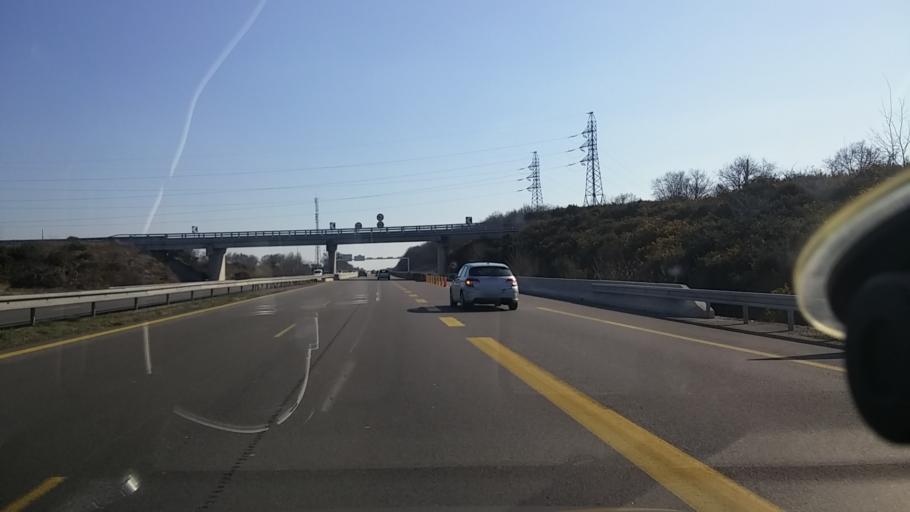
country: FR
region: Centre
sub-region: Departement du Loir-et-Cher
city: Theillay
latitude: 47.2871
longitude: 2.0435
